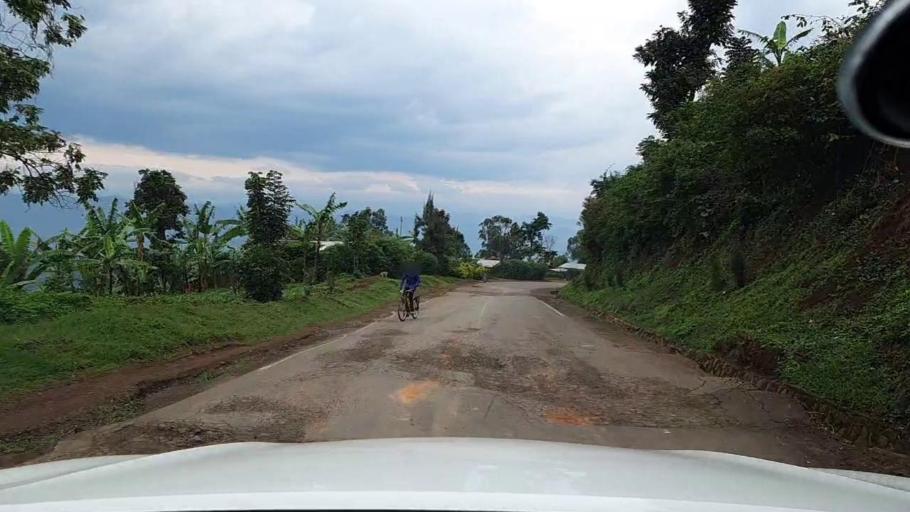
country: RW
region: Western Province
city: Cyangugu
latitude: -2.6516
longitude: 28.9677
